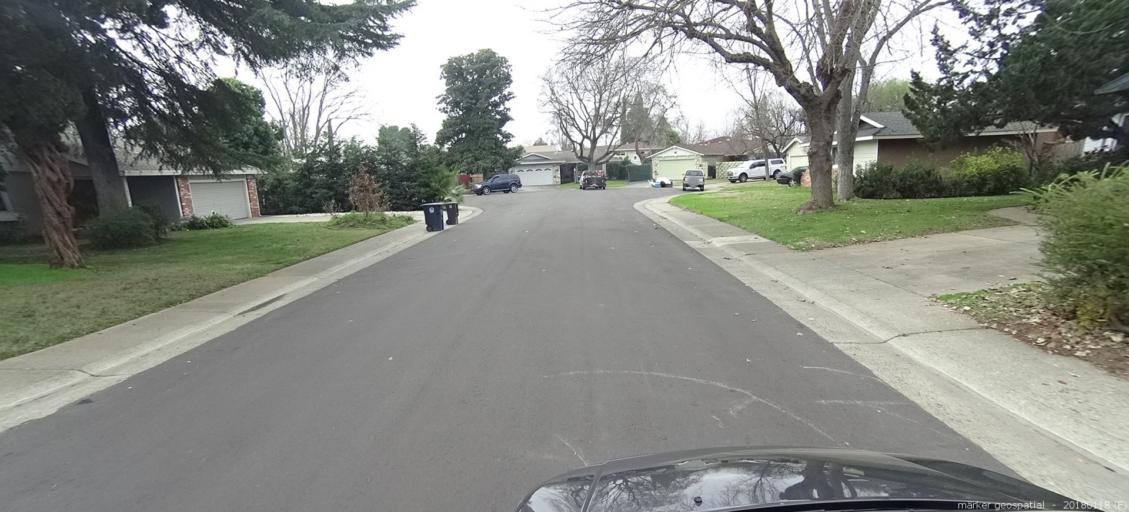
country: US
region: California
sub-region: Sacramento County
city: Rancho Cordova
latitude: 38.5900
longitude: -121.3194
